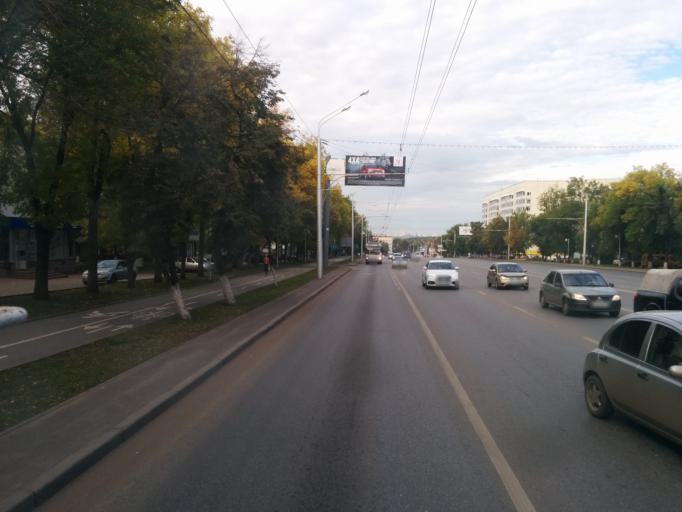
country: RU
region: Bashkortostan
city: Ufa
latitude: 54.7917
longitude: 56.0366
